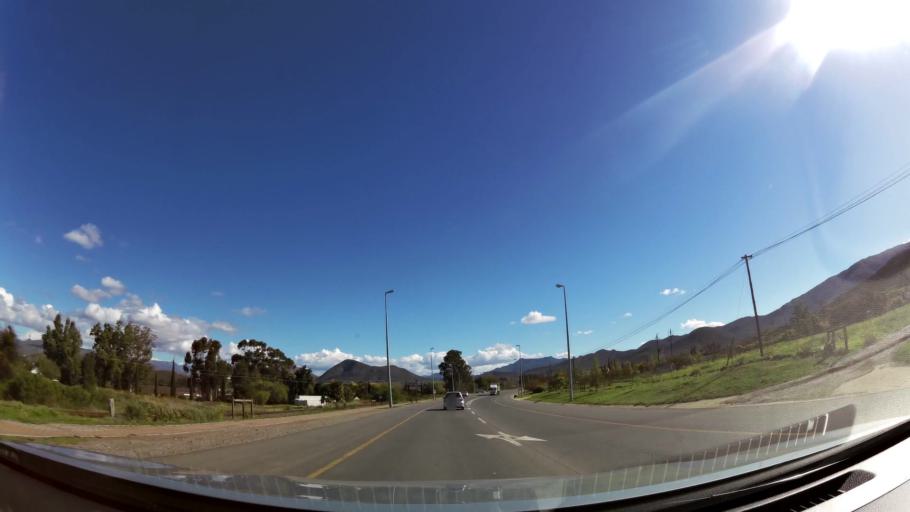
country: ZA
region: Western Cape
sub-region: Cape Winelands District Municipality
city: Ashton
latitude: -33.8048
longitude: 19.8683
